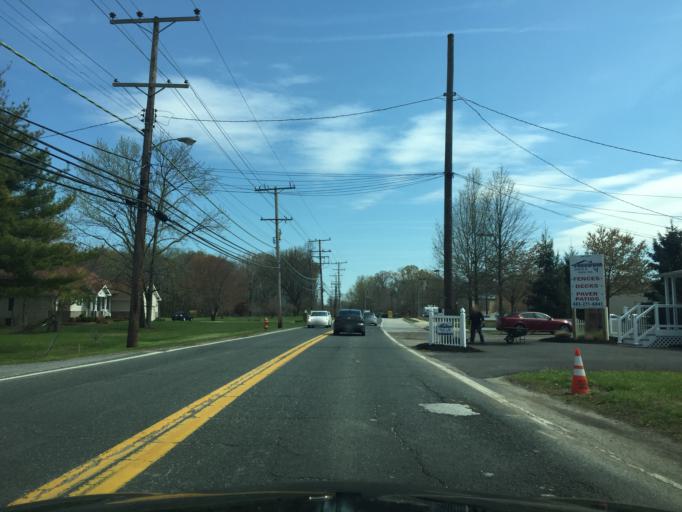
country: US
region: Maryland
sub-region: Baltimore County
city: Middle River
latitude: 39.3001
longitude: -76.4370
